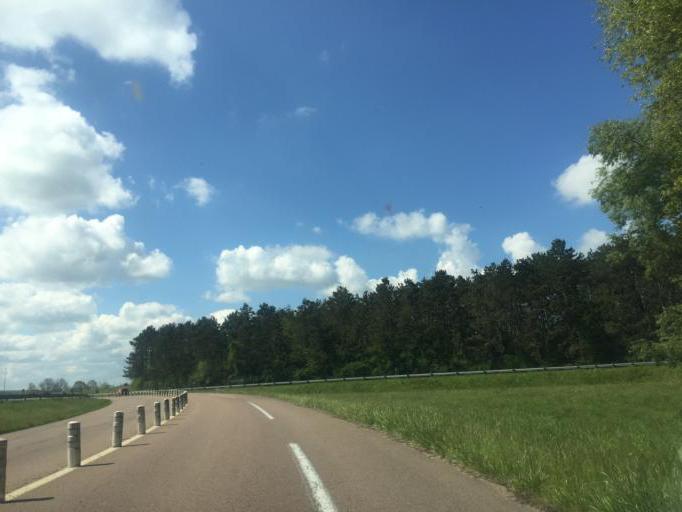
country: FR
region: Bourgogne
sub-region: Departement de l'Yonne
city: Avallon
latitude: 47.5124
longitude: 3.9925
